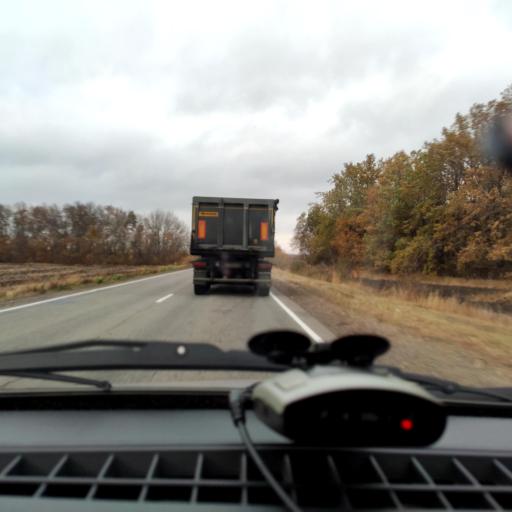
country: RU
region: Voronezj
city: Shilovo
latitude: 51.4405
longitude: 38.9973
